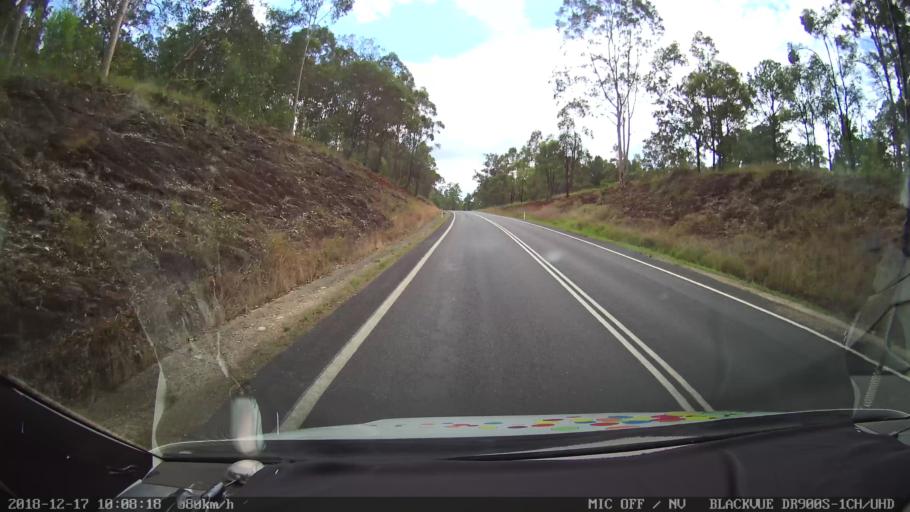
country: AU
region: New South Wales
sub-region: Tenterfield Municipality
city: Carrolls Creek
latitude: -28.8912
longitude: 152.5295
